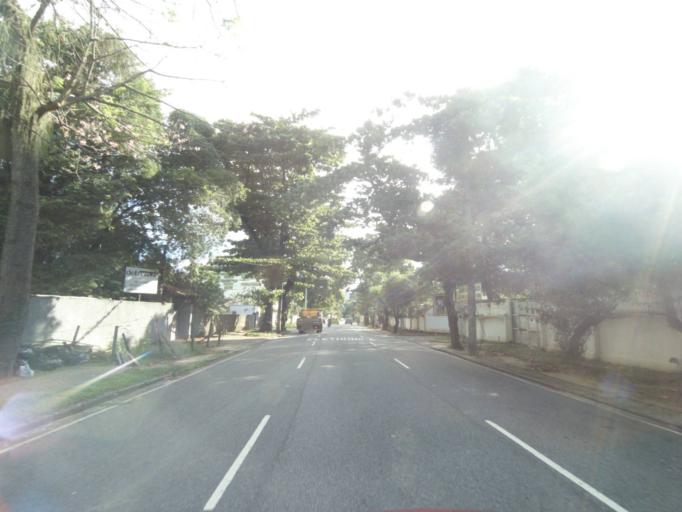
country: BR
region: Rio de Janeiro
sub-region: Rio De Janeiro
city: Rio de Janeiro
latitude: -22.9317
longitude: -43.3278
